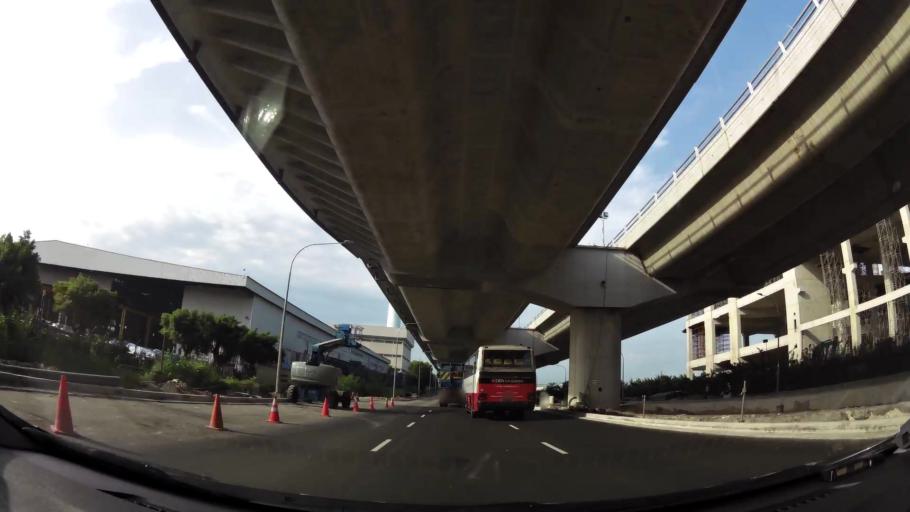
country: MY
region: Johor
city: Johor Bahru
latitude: 1.3278
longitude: 103.6363
